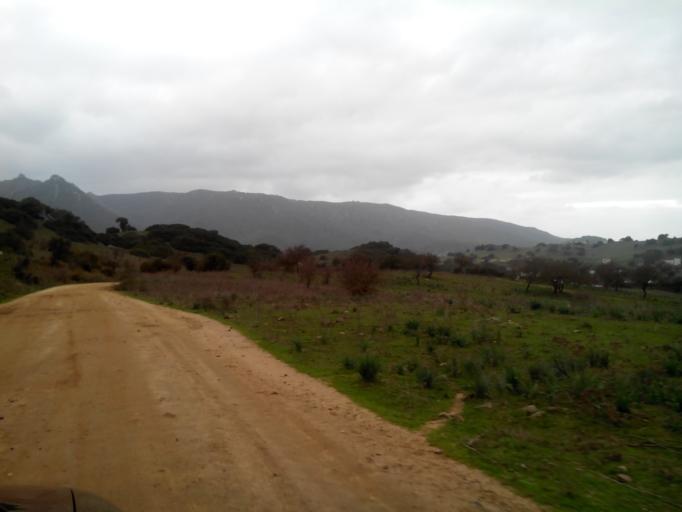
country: IT
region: Sardinia
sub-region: Provincia di Nuoro
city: Austis
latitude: 40.1336
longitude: 9.0376
